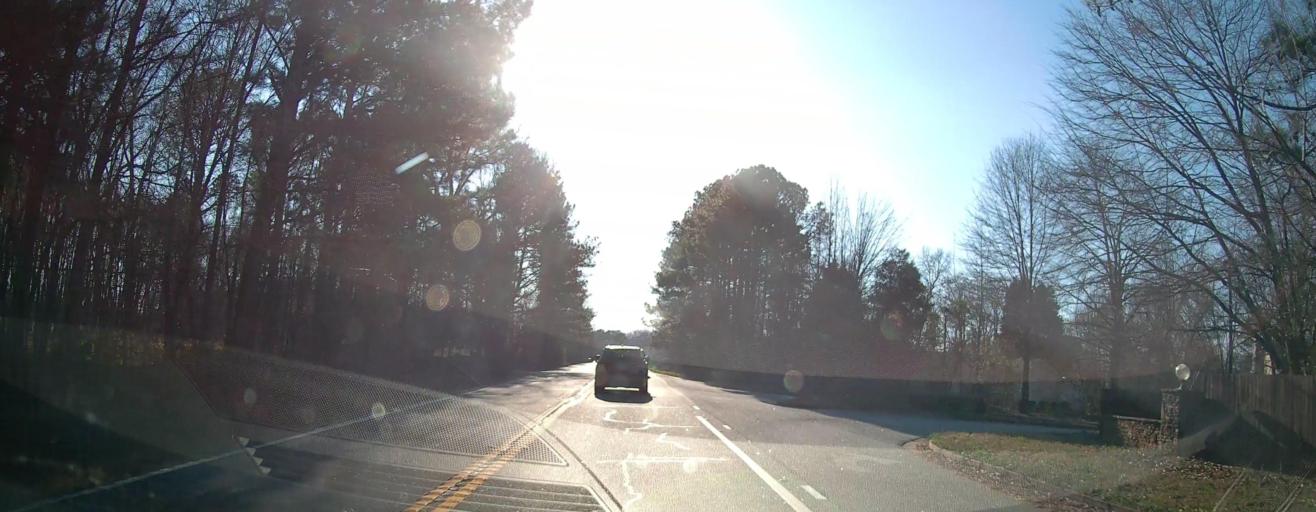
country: US
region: Georgia
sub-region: Henry County
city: Hampton
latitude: 33.4256
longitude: -84.2202
